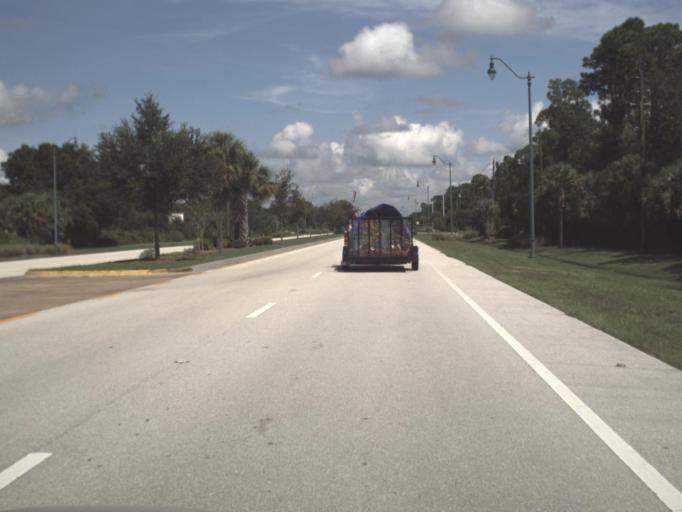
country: US
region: Florida
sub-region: Sarasota County
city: North Port
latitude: 27.0559
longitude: -82.1570
